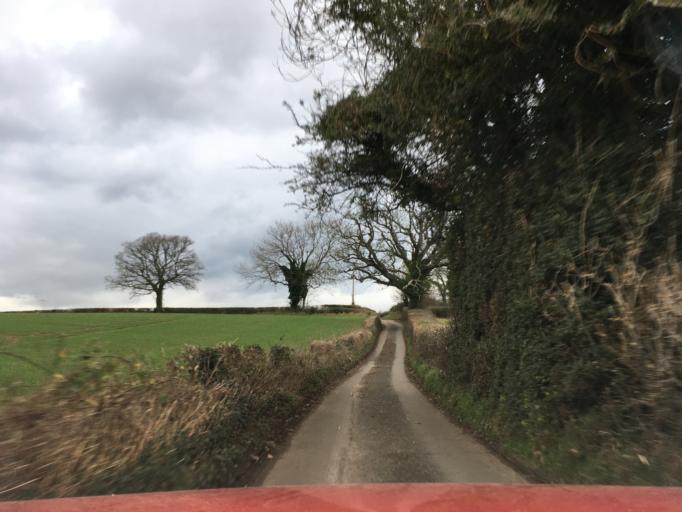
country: GB
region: Wales
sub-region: Newport
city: Llanvaches
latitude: 51.6100
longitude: -2.8052
